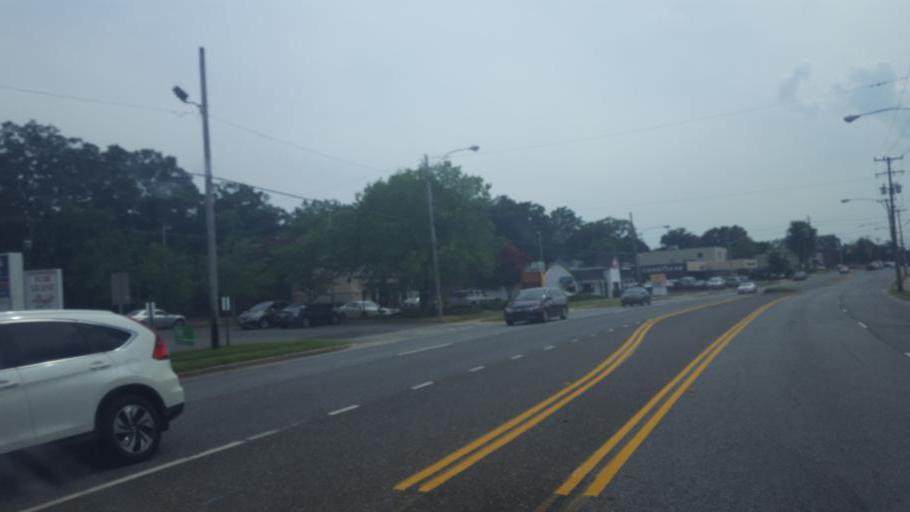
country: US
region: South Carolina
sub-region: York County
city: Rock Hill
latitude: 34.9452
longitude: -81.0263
